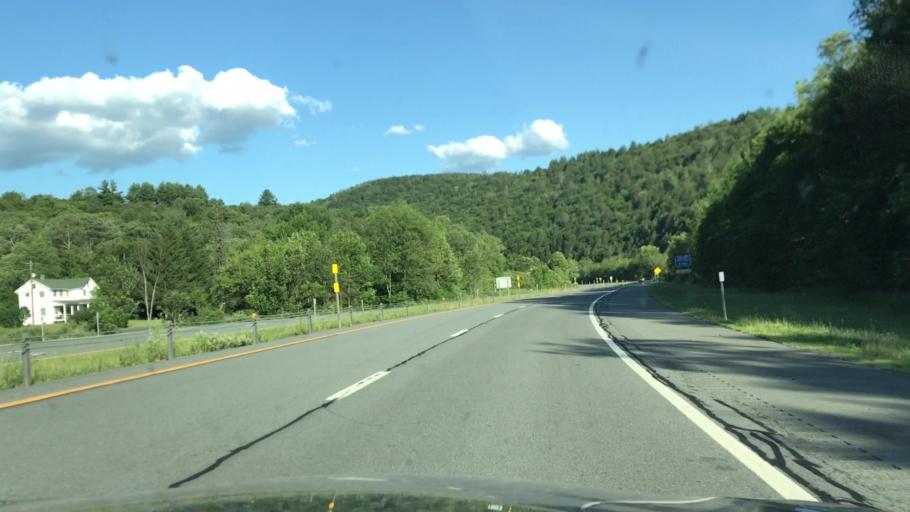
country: US
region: New York
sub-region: Sullivan County
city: Livingston Manor
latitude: 41.9279
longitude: -74.9007
